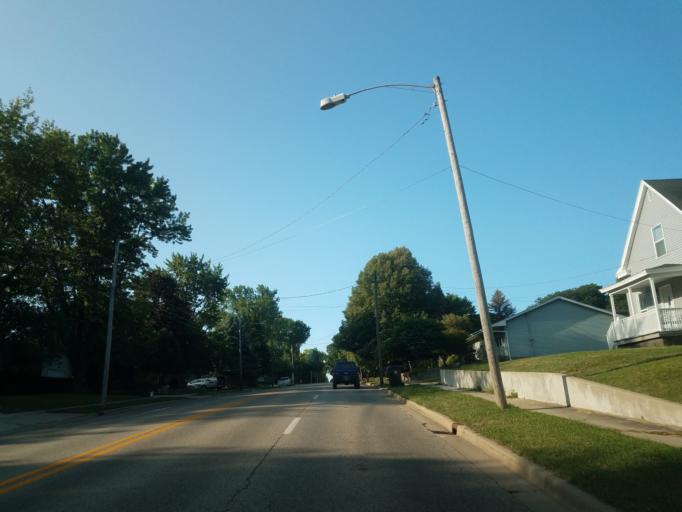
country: US
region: Illinois
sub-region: McLean County
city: Normal
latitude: 40.5016
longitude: -88.9822
